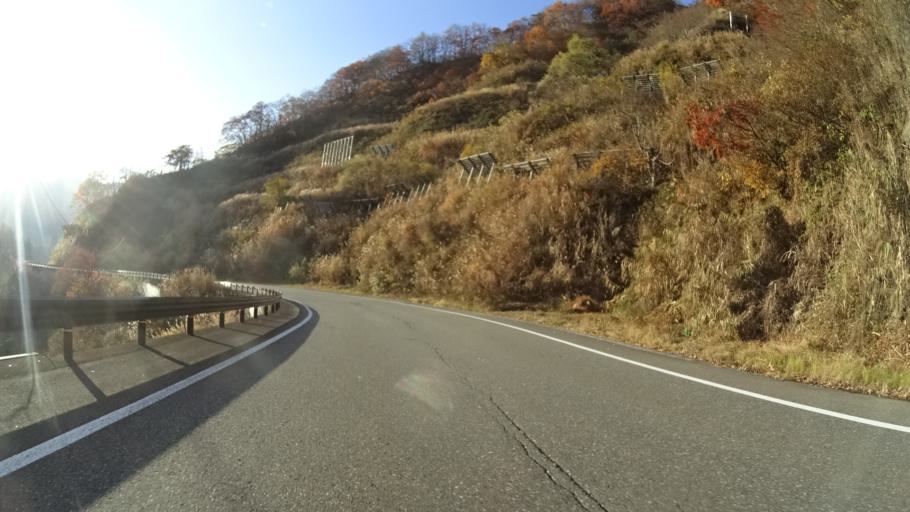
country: JP
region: Niigata
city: Shiozawa
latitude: 36.9848
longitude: 138.7548
